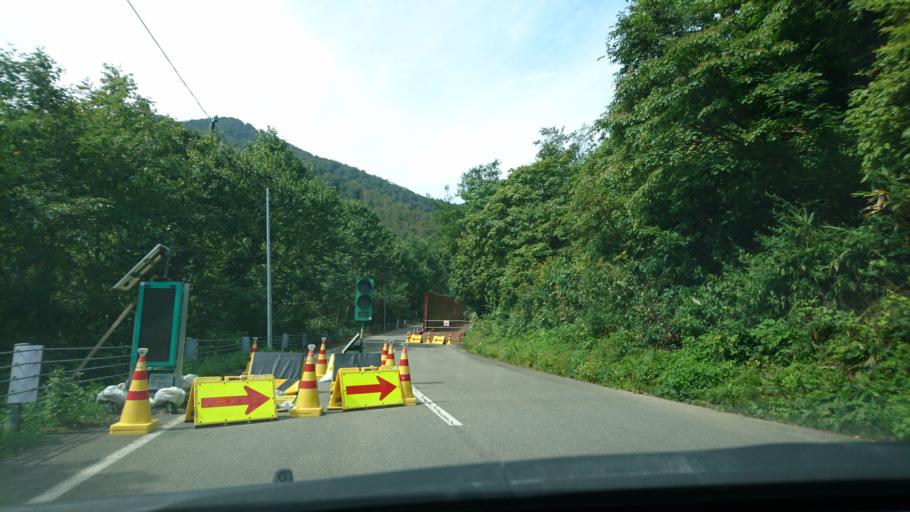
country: JP
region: Akita
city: Yuzawa
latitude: 39.0202
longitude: 140.7293
